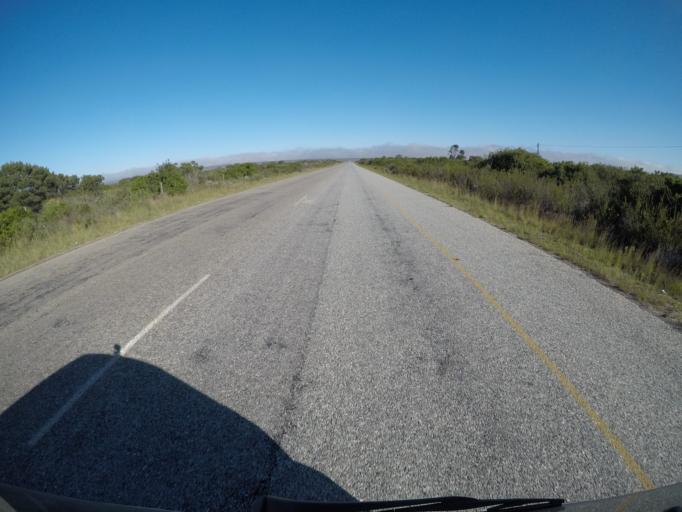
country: ZA
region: Western Cape
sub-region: Eden District Municipality
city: Mossel Bay
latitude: -34.1611
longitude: 22.0099
